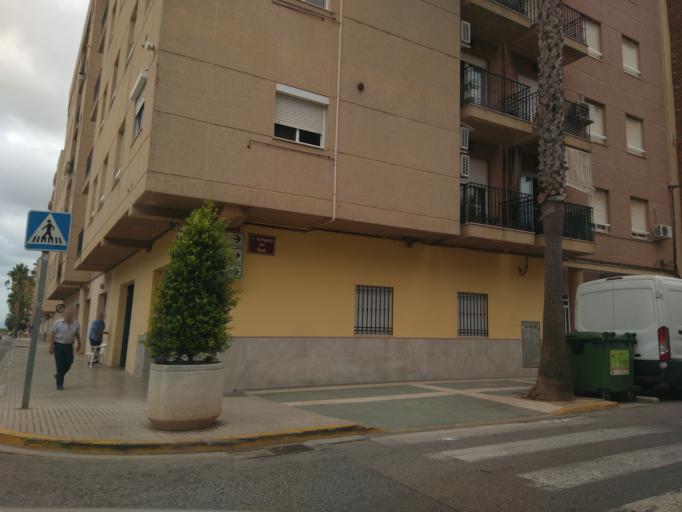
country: ES
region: Valencia
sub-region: Provincia de Valencia
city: Carlet
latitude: 39.2237
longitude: -0.5158
